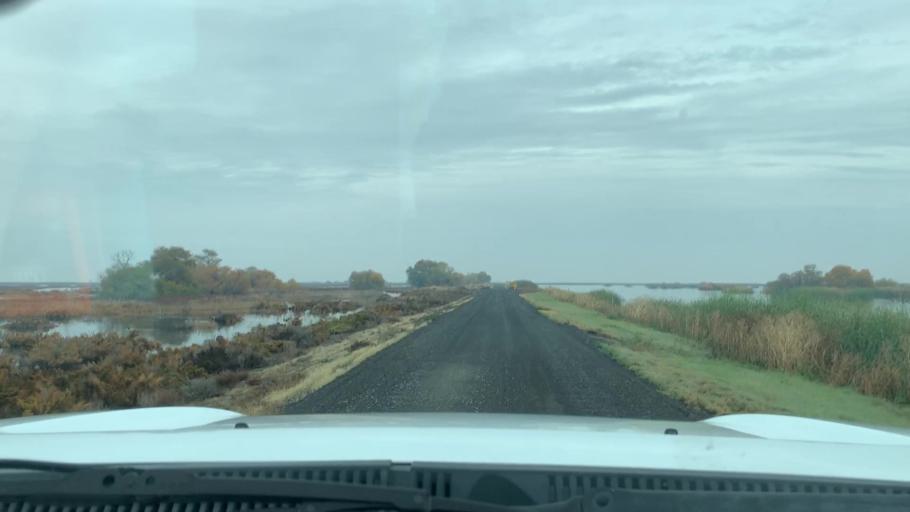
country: US
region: California
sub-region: Kern County
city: Lost Hills
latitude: 35.7493
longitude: -119.5885
